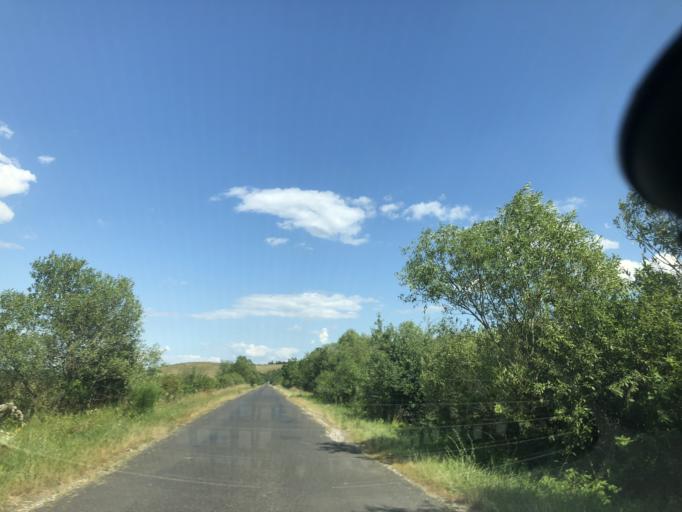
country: HU
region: Borsod-Abauj-Zemplen
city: Szendro
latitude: 48.5418
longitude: 20.7820
